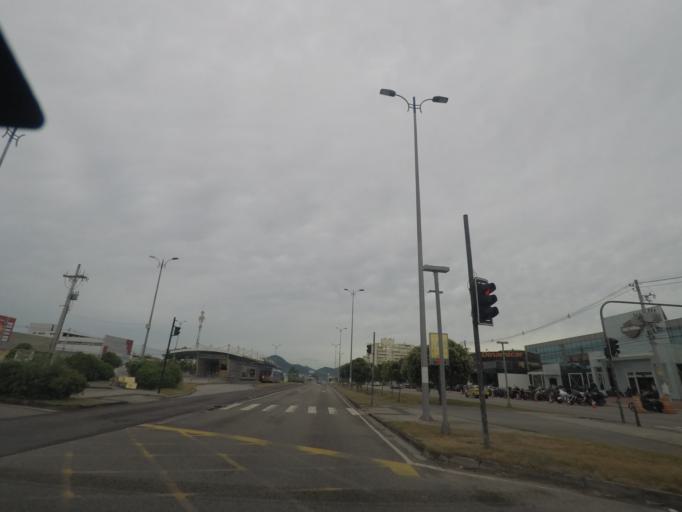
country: BR
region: Rio de Janeiro
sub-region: Nilopolis
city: Nilopolis
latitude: -23.0094
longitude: -43.4479
